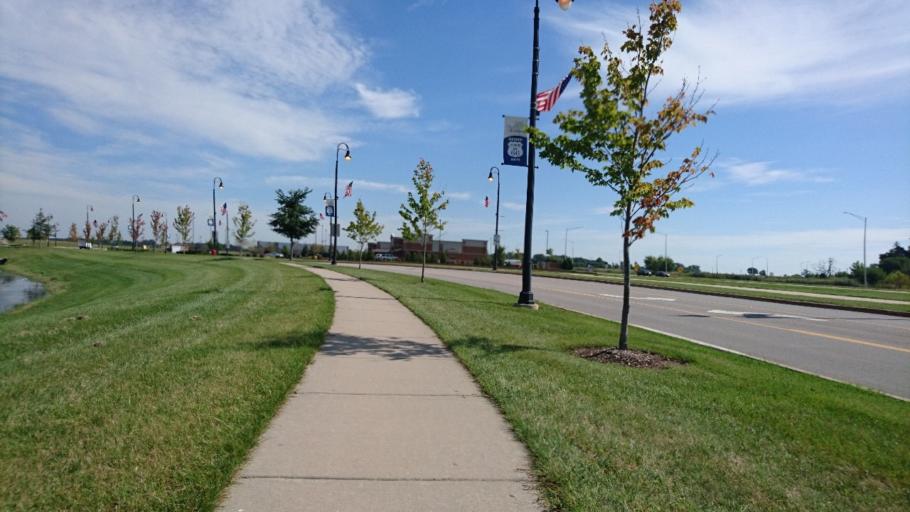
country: US
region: Illinois
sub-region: Will County
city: Elwood
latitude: 41.4044
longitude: -88.1062
